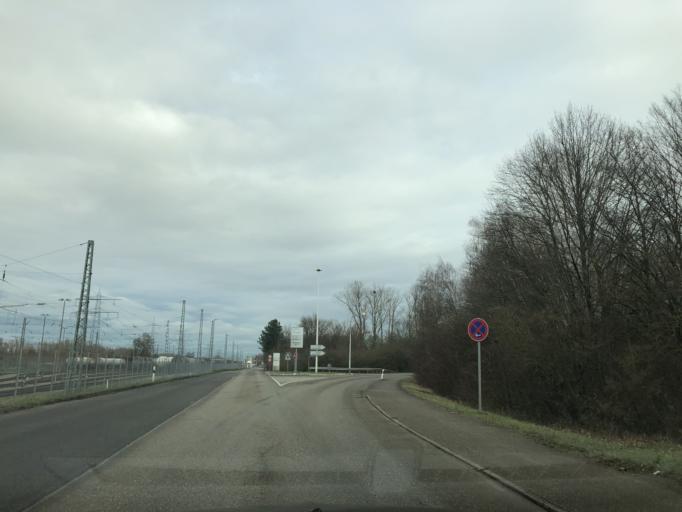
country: DE
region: Rheinland-Pfalz
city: Neupotz
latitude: 49.0493
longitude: 8.3314
